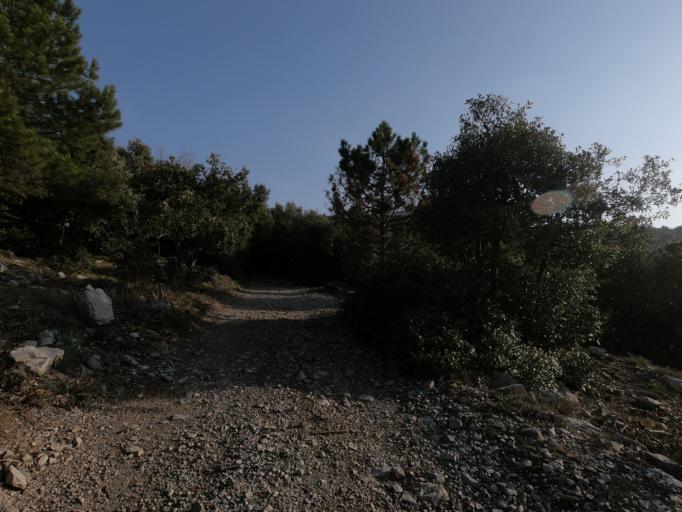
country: IT
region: Liguria
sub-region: Provincia di Savona
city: Cisano
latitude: 44.1045
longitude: 8.1565
